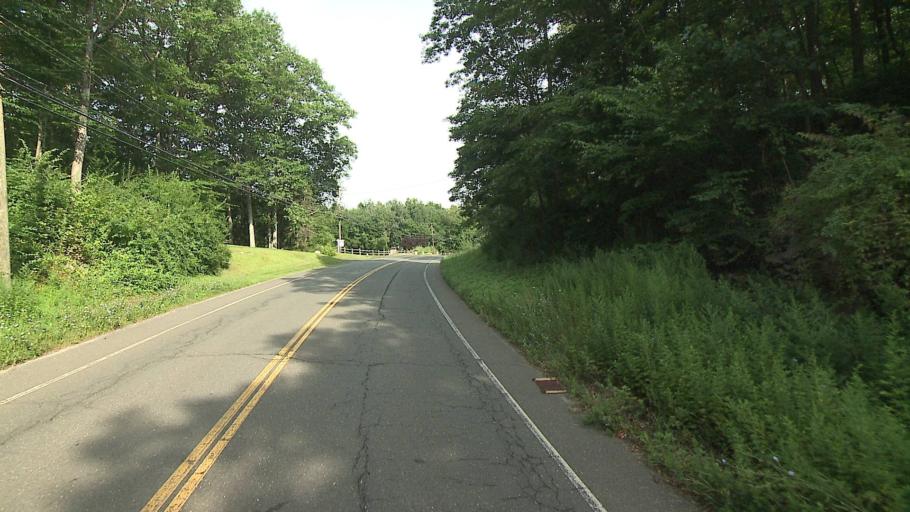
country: US
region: New York
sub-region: Putnam County
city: Putnam Lake
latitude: 41.4738
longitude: -73.4965
